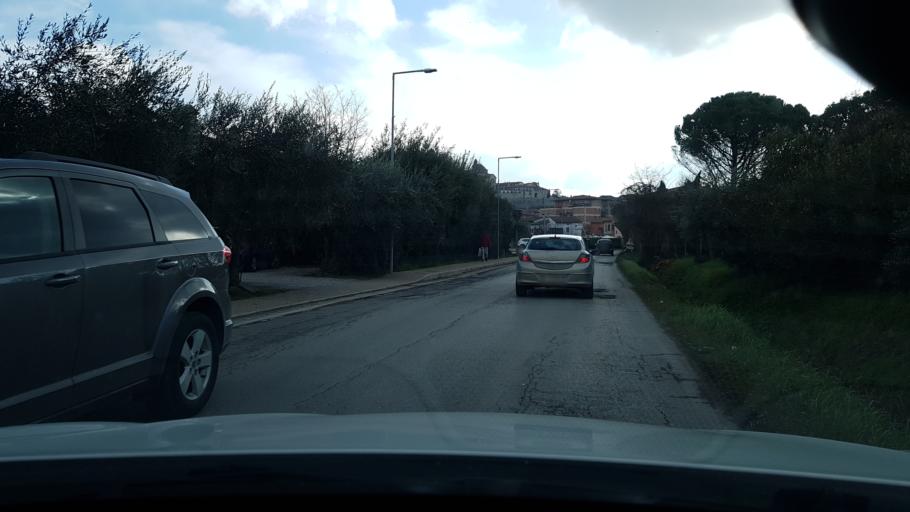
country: IT
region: Umbria
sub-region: Provincia di Perugia
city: Castiglione del Lago
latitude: 43.1299
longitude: 12.0435
